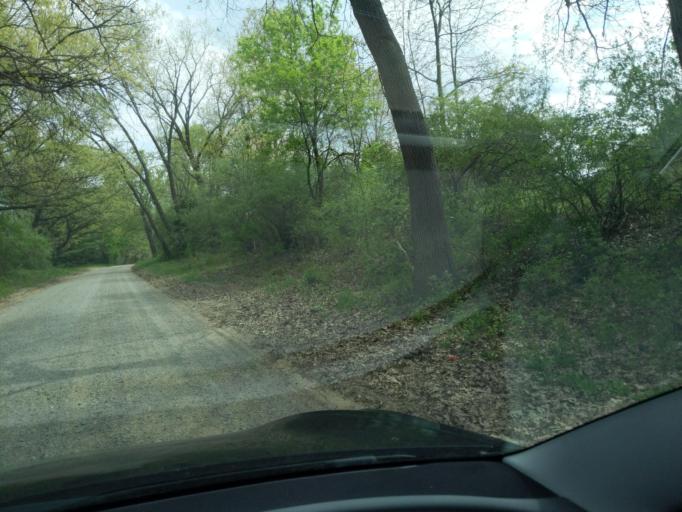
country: US
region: Michigan
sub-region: Washtenaw County
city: Chelsea
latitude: 42.4185
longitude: -84.0617
